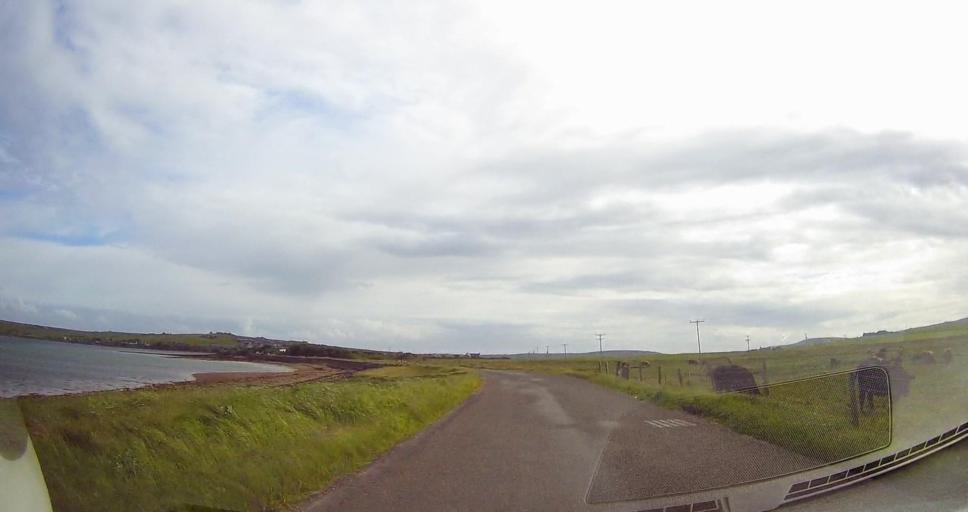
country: GB
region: Scotland
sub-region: Orkney Islands
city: Stromness
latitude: 58.8105
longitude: -3.2024
